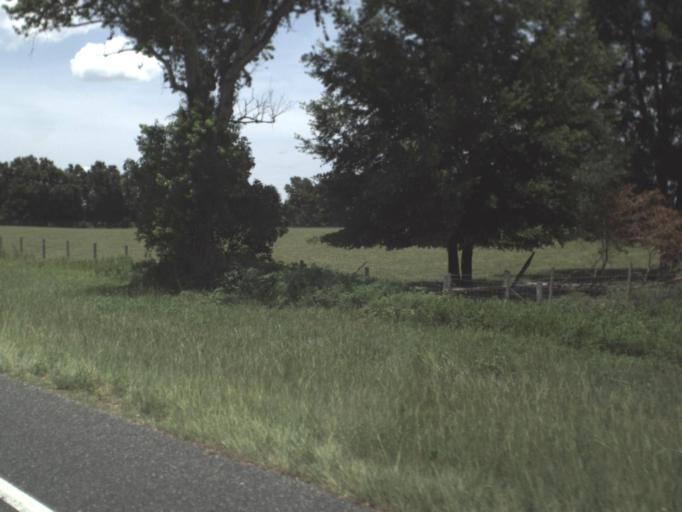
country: US
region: Florida
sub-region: Levy County
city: Chiefland
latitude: 29.5146
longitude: -82.8227
